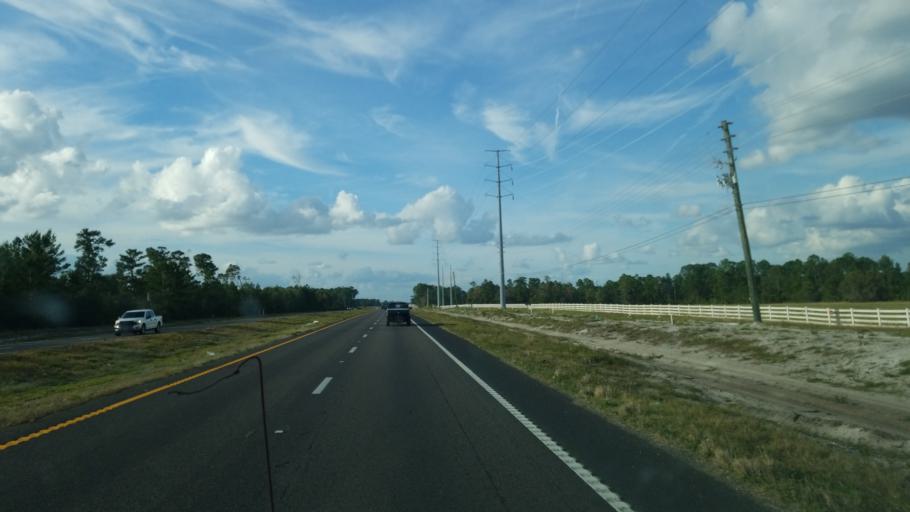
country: US
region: Florida
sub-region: Osceola County
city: Saint Cloud
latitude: 28.2139
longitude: -81.1752
